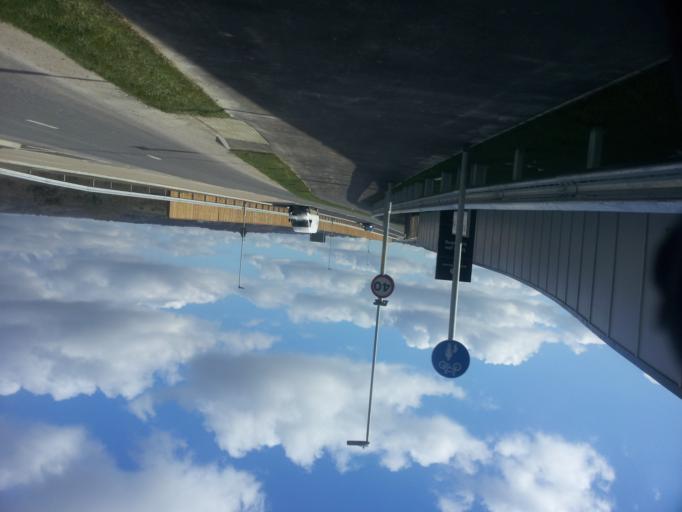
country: GB
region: England
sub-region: Medway
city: Halling
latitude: 51.3417
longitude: 0.4572
